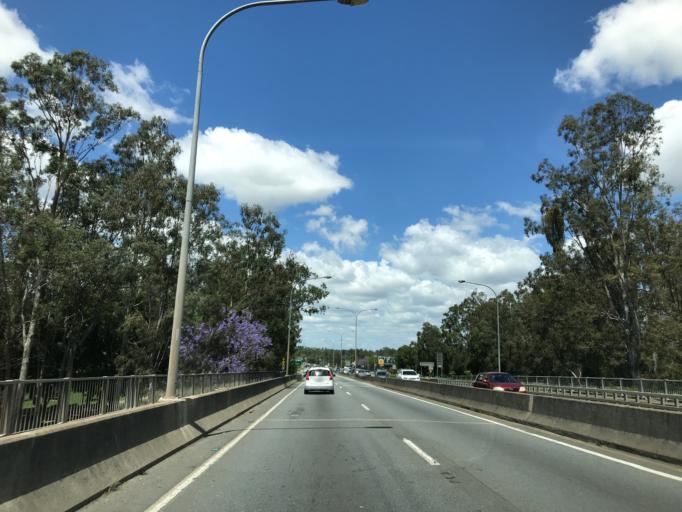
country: AU
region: Queensland
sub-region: Brisbane
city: Seventeen Mile Rocks
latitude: -27.5281
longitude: 152.9470
